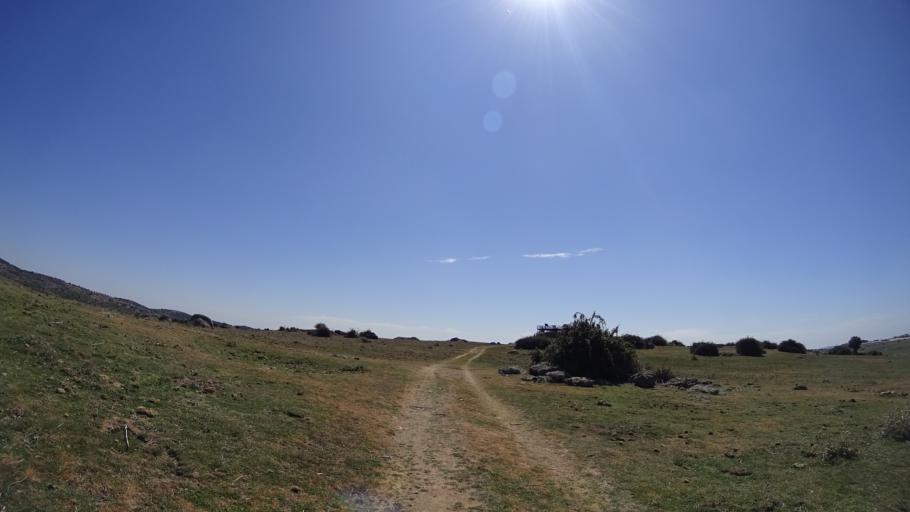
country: ES
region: Madrid
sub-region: Provincia de Madrid
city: Colmenar Viejo
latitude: 40.7070
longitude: -3.7499
